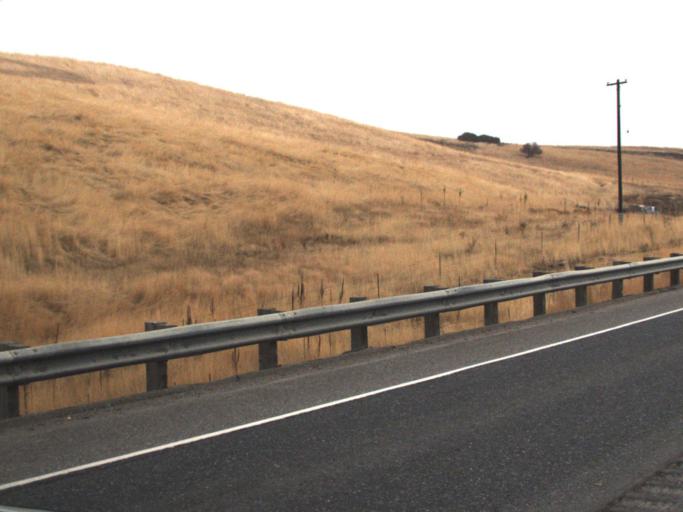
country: US
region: Washington
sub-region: Stevens County
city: Kettle Falls
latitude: 48.6069
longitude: -118.0301
